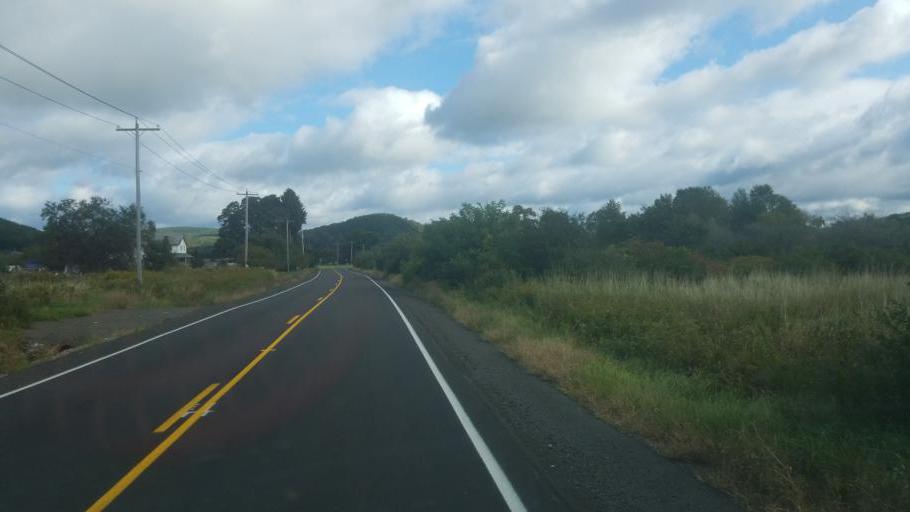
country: US
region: New York
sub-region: Cattaraugus County
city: Weston Mills
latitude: 42.0820
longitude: -78.3683
